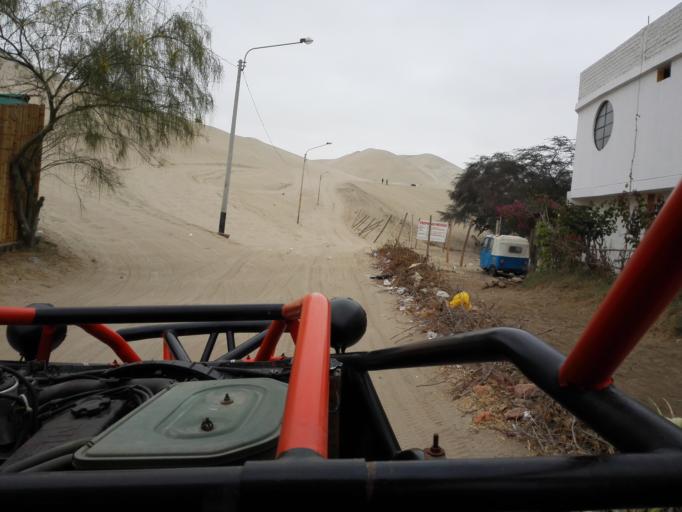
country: PE
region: Ica
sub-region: Provincia de Ica
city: Ica
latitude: -14.0888
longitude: -75.7637
